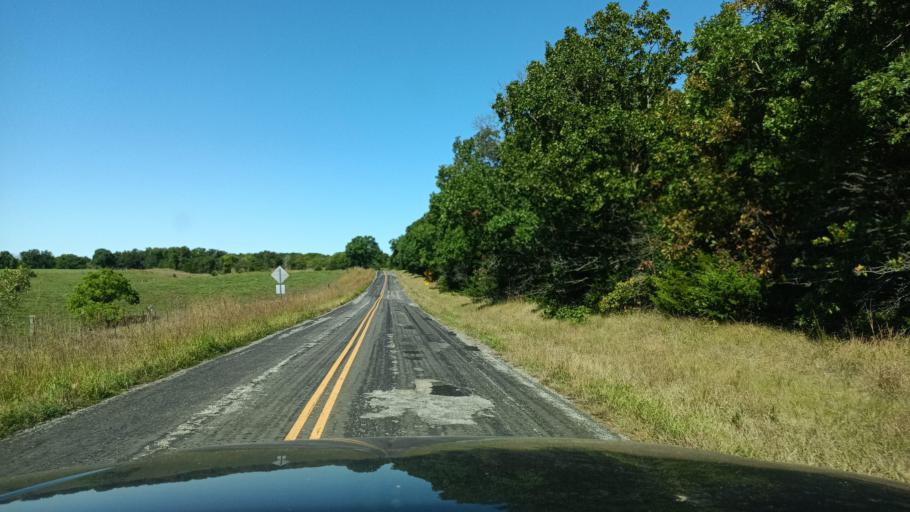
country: US
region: Missouri
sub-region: Scotland County
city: Memphis
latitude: 40.3522
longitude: -92.3446
